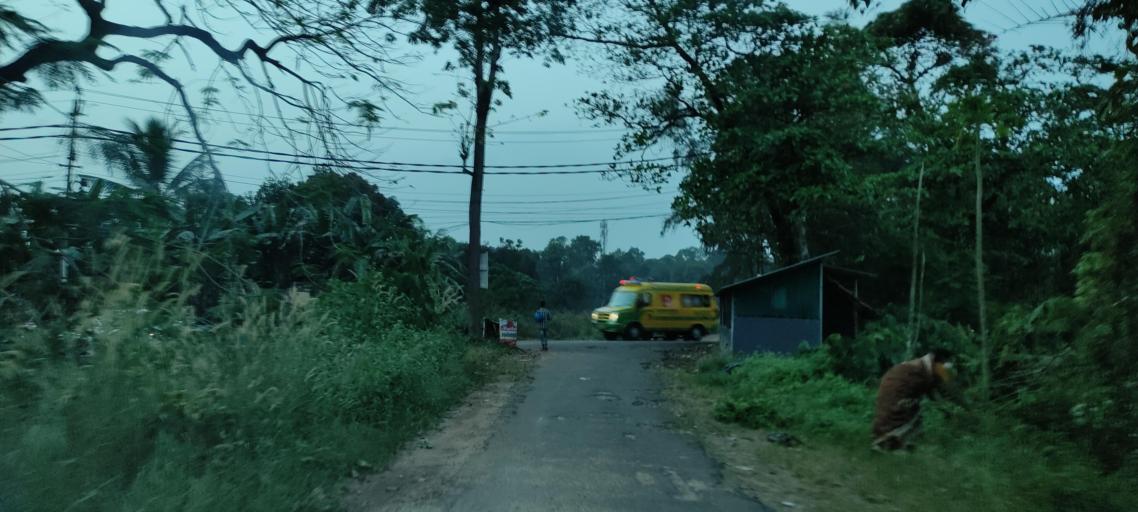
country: IN
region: Kerala
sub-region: Pattanamtitta
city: Adur
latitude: 9.1621
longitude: 76.7444
